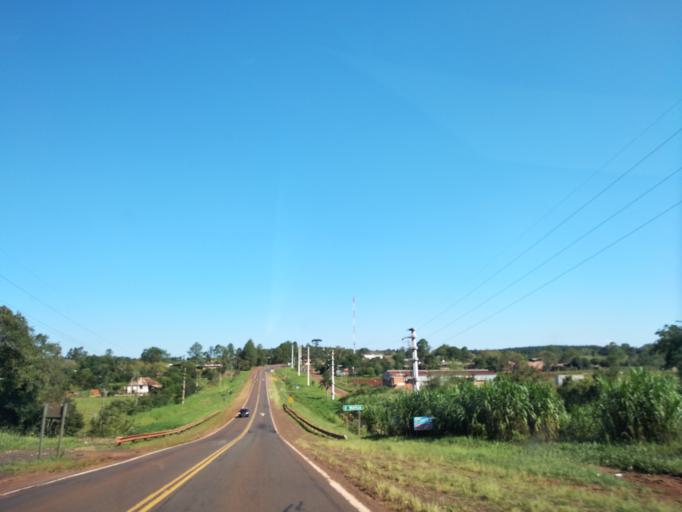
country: AR
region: Misiones
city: Puerto Rico
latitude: -26.8605
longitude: -55.0456
